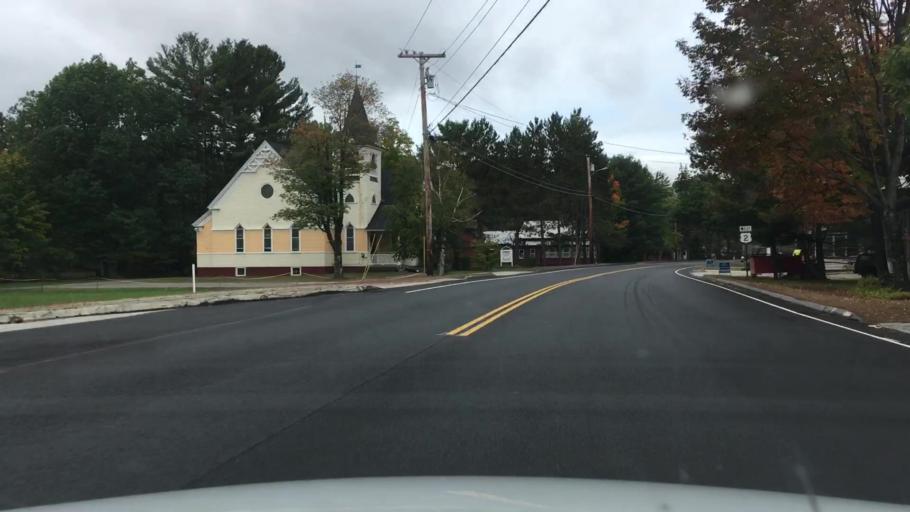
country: US
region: Maine
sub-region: Oxford County
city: Bethel
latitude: 44.4019
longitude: -70.8614
